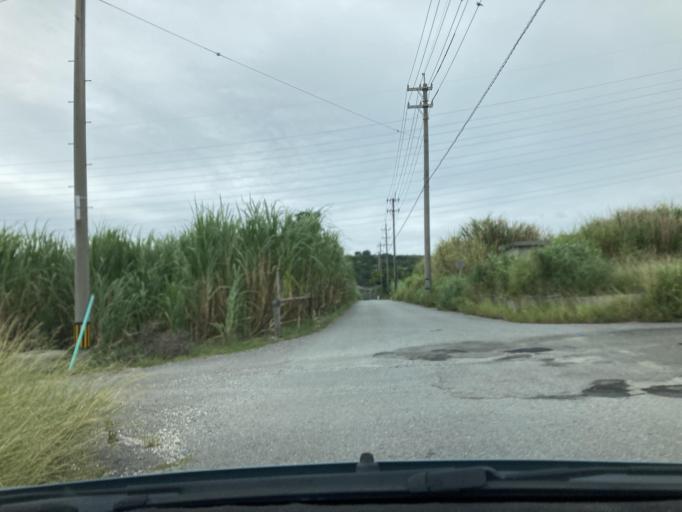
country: JP
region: Okinawa
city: Tomigusuku
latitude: 26.1701
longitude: 127.7112
